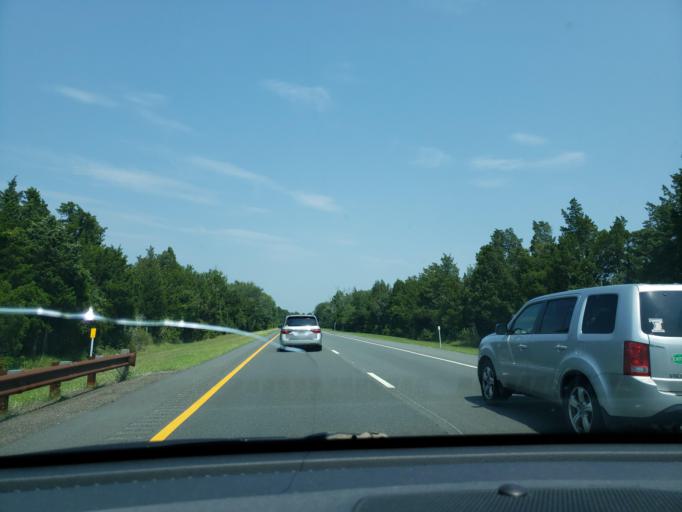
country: US
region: New Jersey
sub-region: Cape May County
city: Sea Isle City
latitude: 39.1603
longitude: -74.7408
